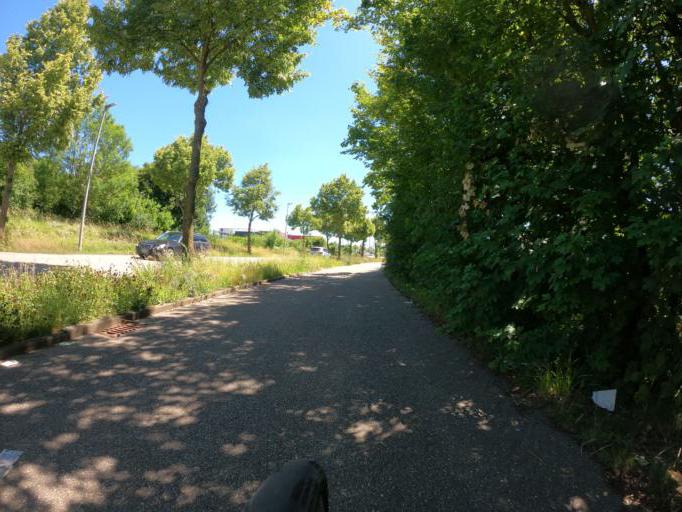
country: DE
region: Baden-Wuerttemberg
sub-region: Regierungsbezirk Stuttgart
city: Vaihingen an der Enz
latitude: 48.9419
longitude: 8.9628
